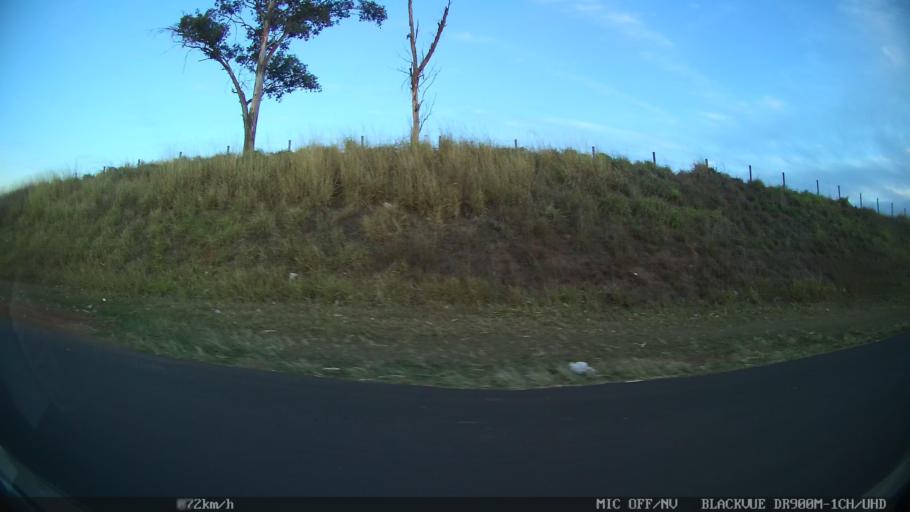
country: BR
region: Sao Paulo
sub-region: Catanduva
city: Catanduva
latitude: -21.1321
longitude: -49.0163
